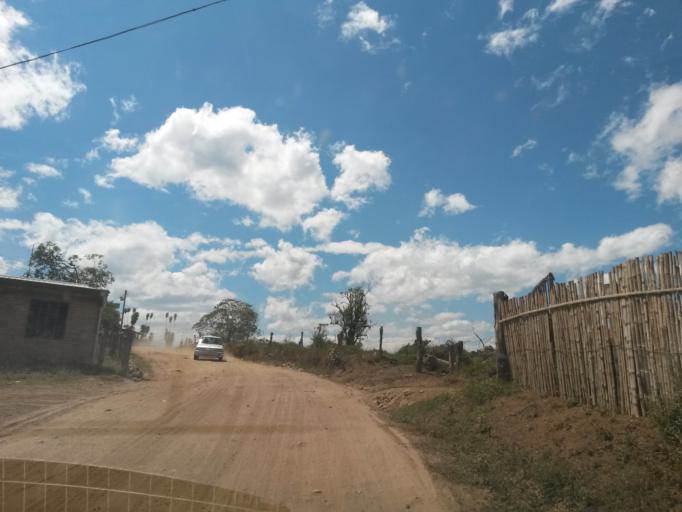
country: CO
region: Cauca
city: Morales
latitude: 2.7459
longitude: -76.6281
